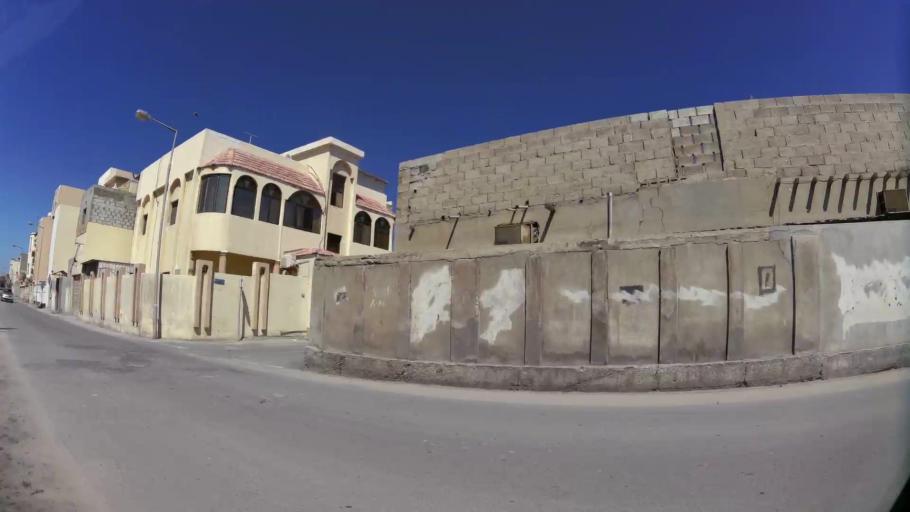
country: BH
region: Muharraq
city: Al Muharraq
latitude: 26.2795
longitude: 50.6338
